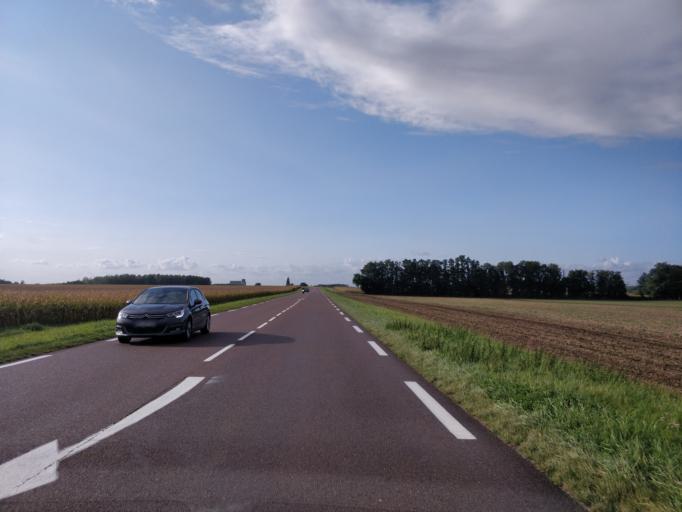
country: FR
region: Champagne-Ardenne
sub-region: Departement de l'Aube
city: Lusigny-sur-Barse
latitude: 48.2737
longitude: 4.2037
